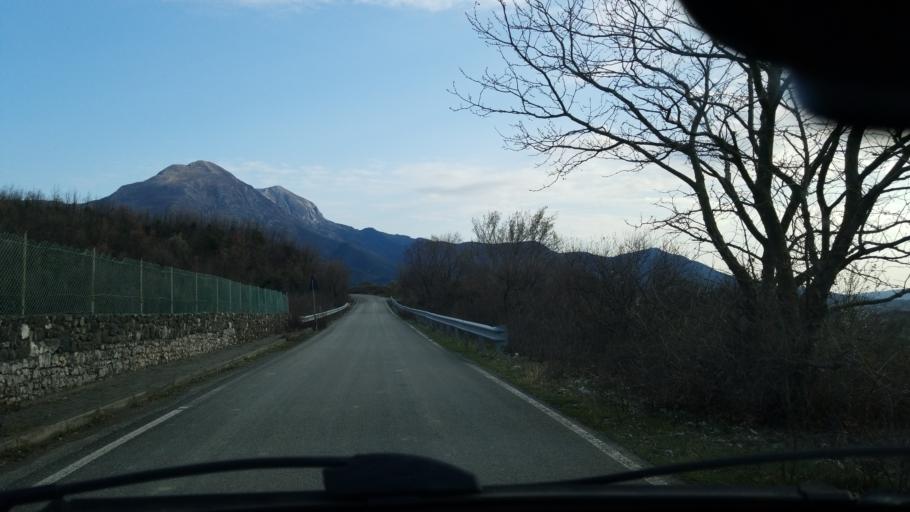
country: AL
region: Lezhe
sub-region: Rrethi i Lezhes
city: Kallmeti i Madh
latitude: 41.8800
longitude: 19.6923
